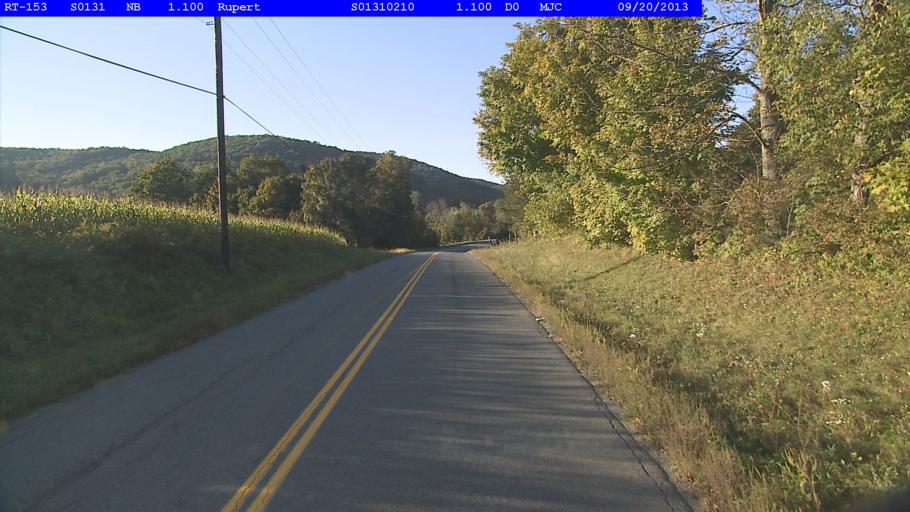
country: US
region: New York
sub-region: Washington County
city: Granville
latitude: 43.2711
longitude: -73.2361
